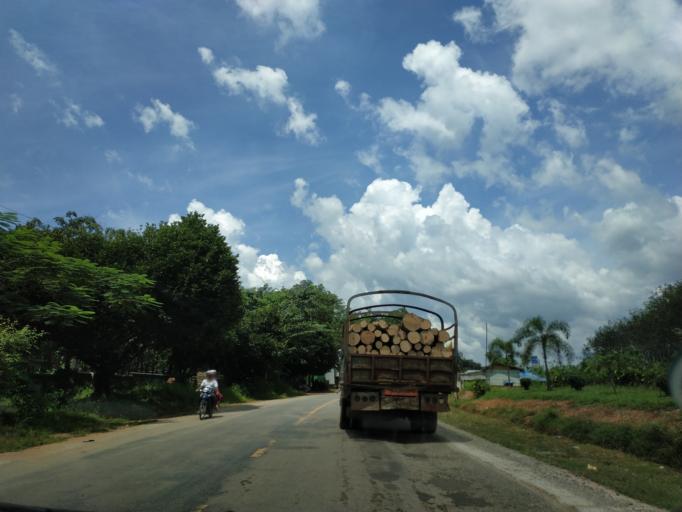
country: TH
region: Kanchanaburi
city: Sangkhla Buri
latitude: 15.2686
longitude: 97.8566
